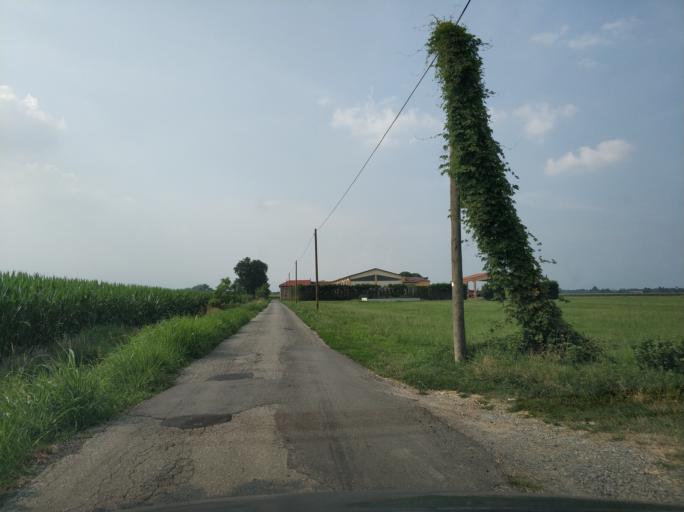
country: IT
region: Piedmont
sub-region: Provincia di Torino
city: Leini
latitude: 45.1905
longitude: 7.6862
